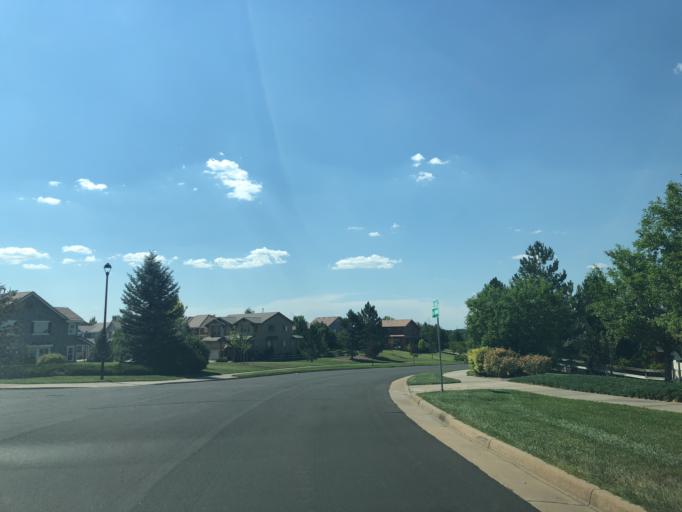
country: US
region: Colorado
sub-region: Arapahoe County
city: Dove Valley
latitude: 39.6059
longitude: -104.7837
